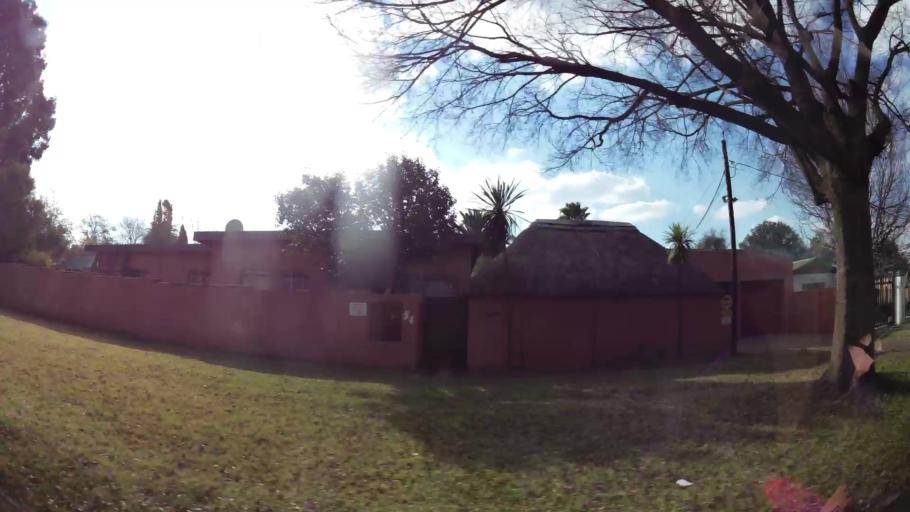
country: ZA
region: Gauteng
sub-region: West Rand District Municipality
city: Krugersdorp
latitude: -26.0887
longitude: 27.7749
